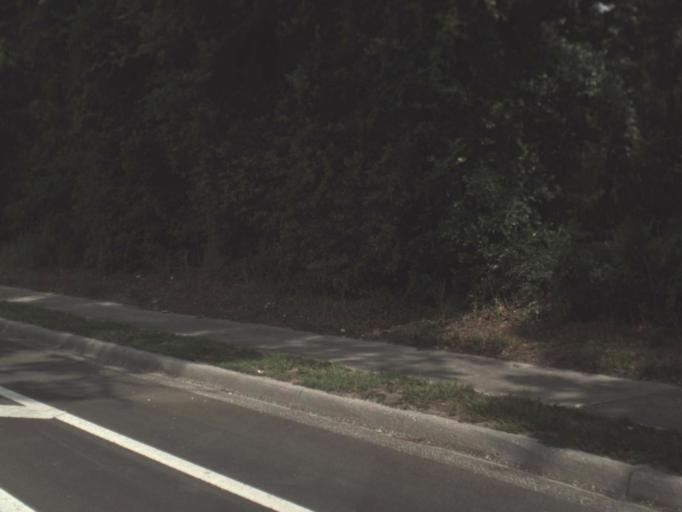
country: US
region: Florida
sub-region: Alachua County
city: Gainesville
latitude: 29.6415
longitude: -82.2861
